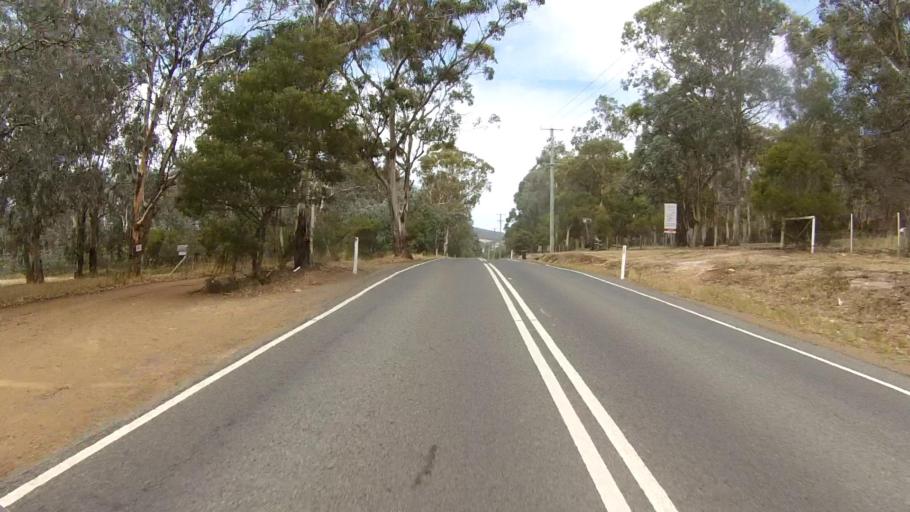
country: AU
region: Tasmania
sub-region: Clarence
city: Lauderdale
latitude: -42.8976
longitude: 147.4805
